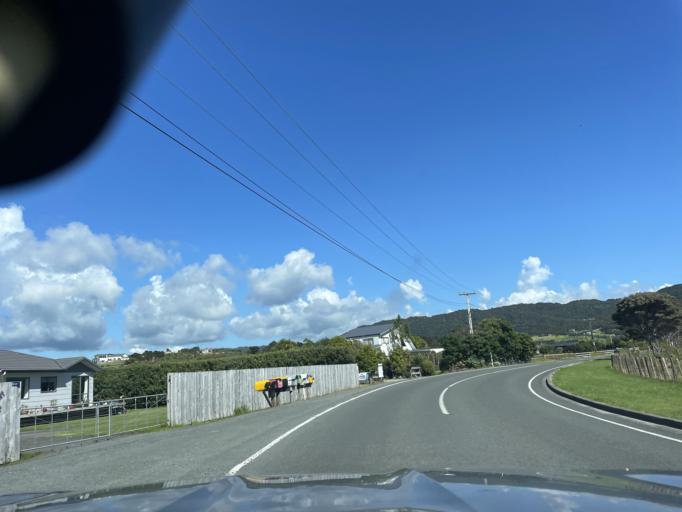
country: NZ
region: Auckland
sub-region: Auckland
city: Wellsford
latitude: -36.0849
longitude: 174.5741
